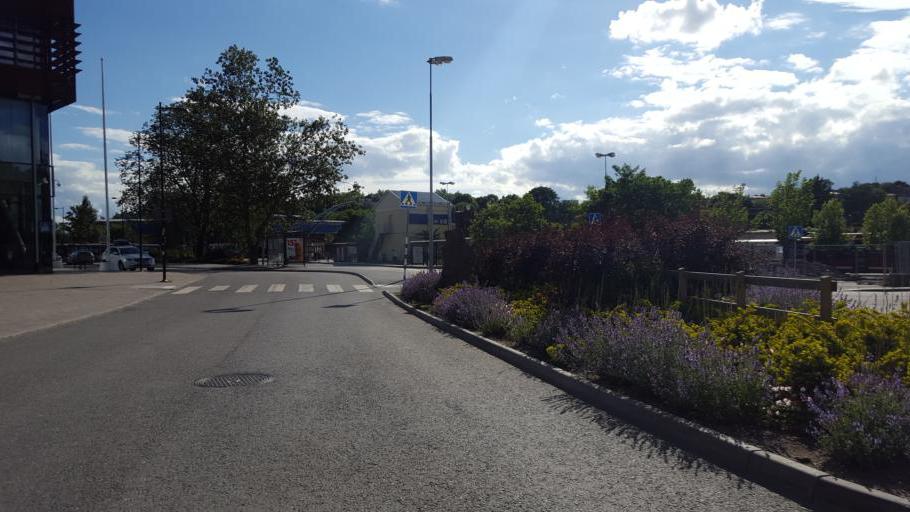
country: SE
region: Stockholm
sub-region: Upplands Vasby Kommun
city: Upplands Vaesby
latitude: 59.5216
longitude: 17.9016
